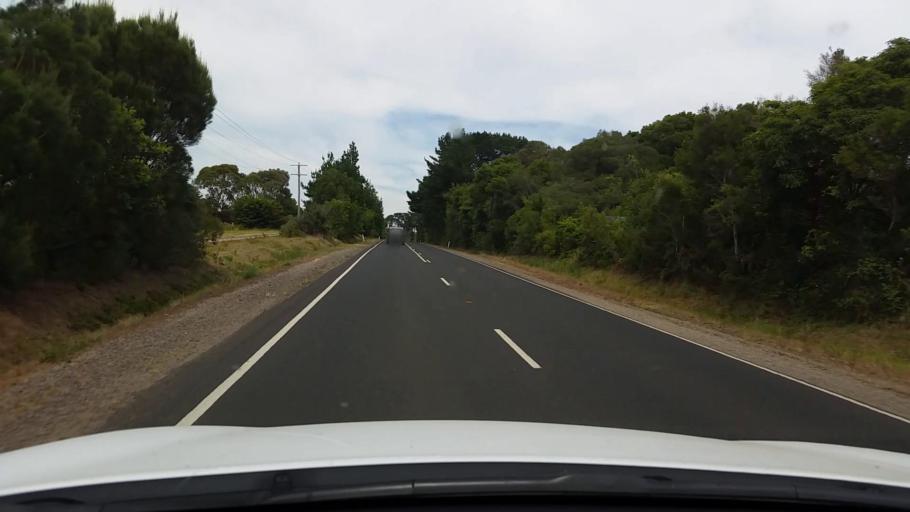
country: AU
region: Victoria
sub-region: Mornington Peninsula
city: Merricks
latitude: -38.4111
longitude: 145.0590
